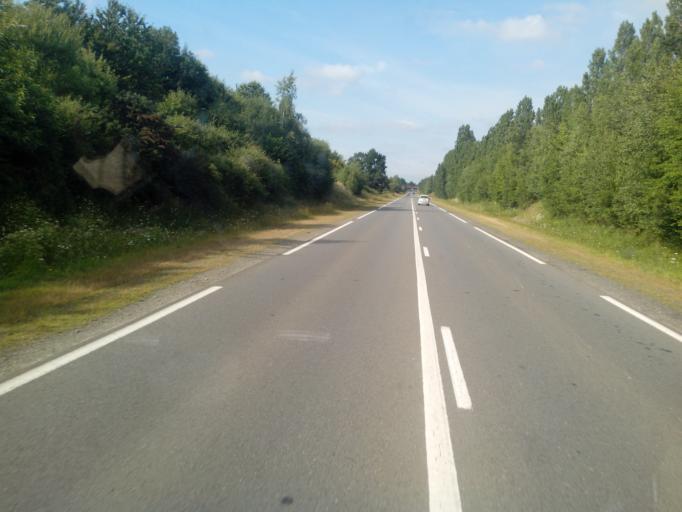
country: FR
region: Brittany
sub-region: Departement d'Ille-et-Vilaine
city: Le Rheu
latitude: 48.0929
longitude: -1.7916
